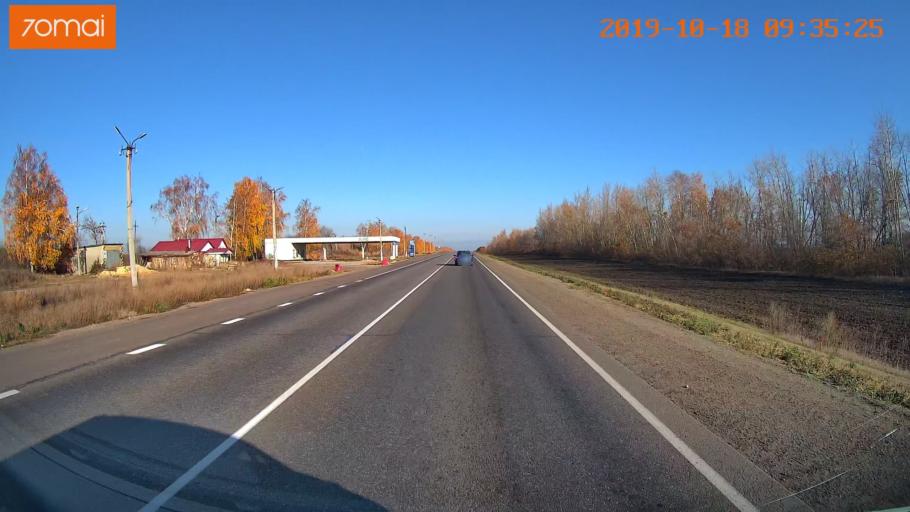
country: RU
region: Tula
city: Yefremov
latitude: 53.1922
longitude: 38.1486
